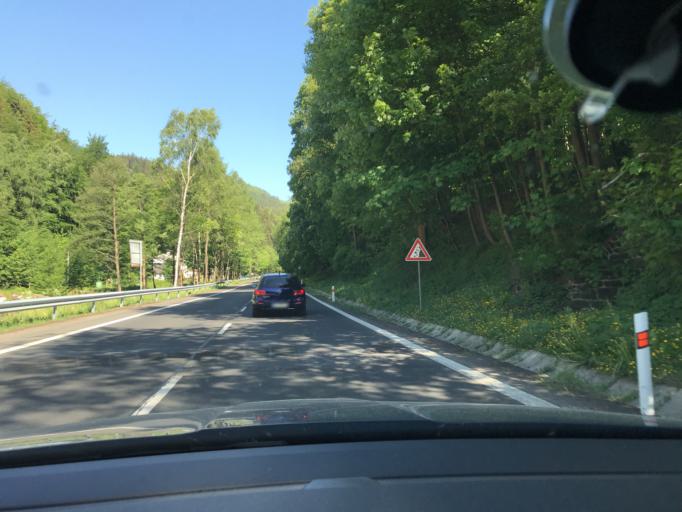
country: CZ
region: Karlovarsky
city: Jachymov
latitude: 50.3429
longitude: 12.9357
